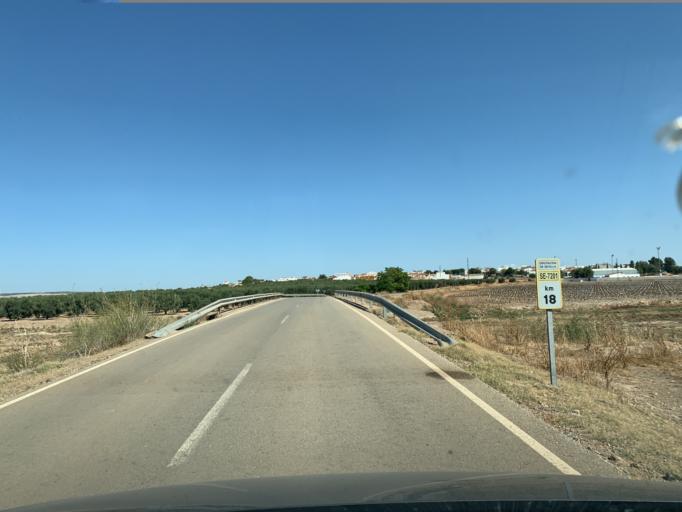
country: ES
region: Andalusia
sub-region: Provincia de Sevilla
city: La Lantejuela
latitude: 37.3497
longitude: -5.2377
